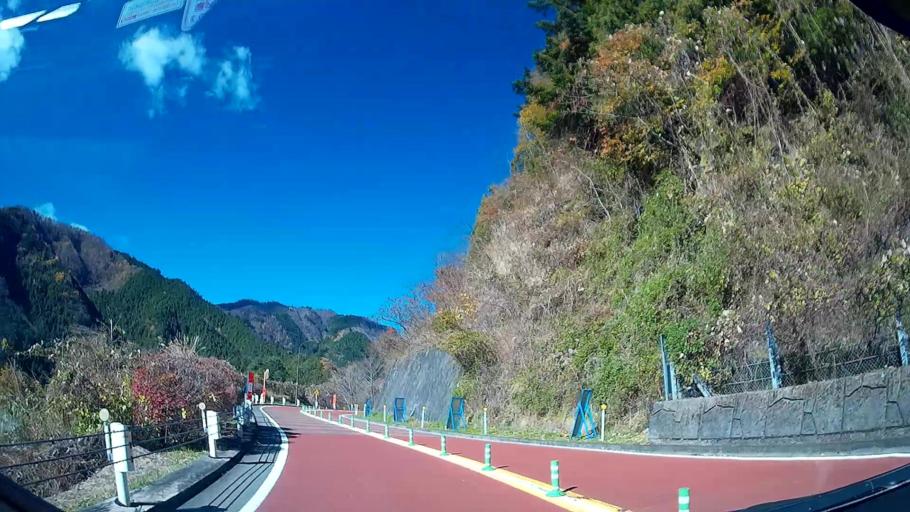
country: JP
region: Yamanashi
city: Uenohara
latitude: 35.7309
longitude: 139.0430
